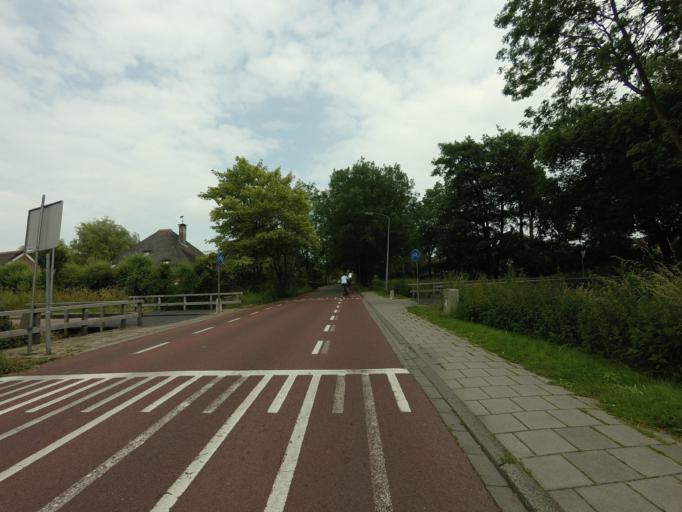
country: NL
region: North Holland
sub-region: Gemeente Hoorn
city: Hoorn
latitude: 52.6626
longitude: 5.0552
